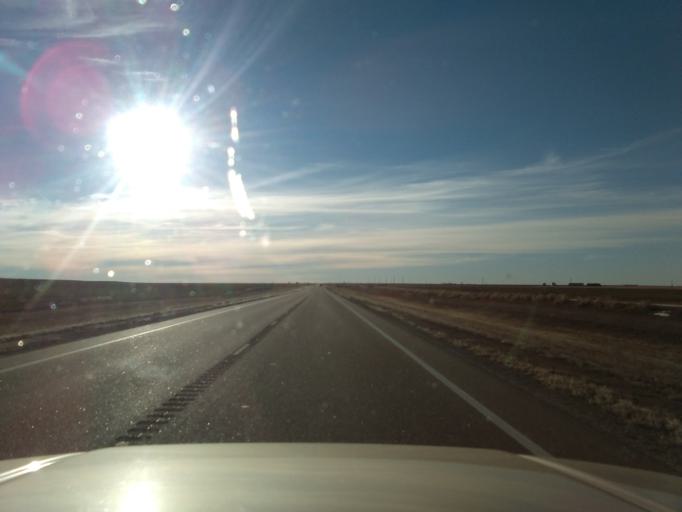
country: US
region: Kansas
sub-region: Sheridan County
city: Hoxie
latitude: 39.5129
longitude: -100.6400
